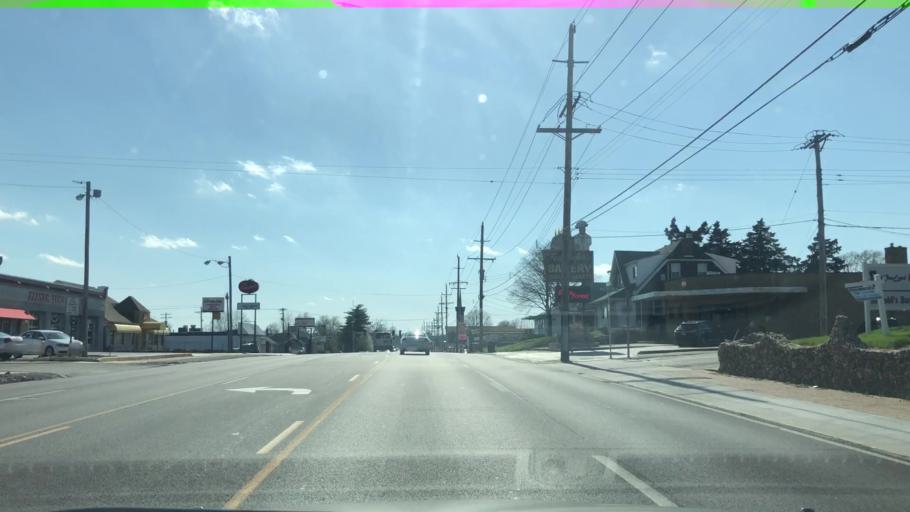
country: US
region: Missouri
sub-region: Saint Louis County
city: Saint George
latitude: 38.5557
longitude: -90.3123
